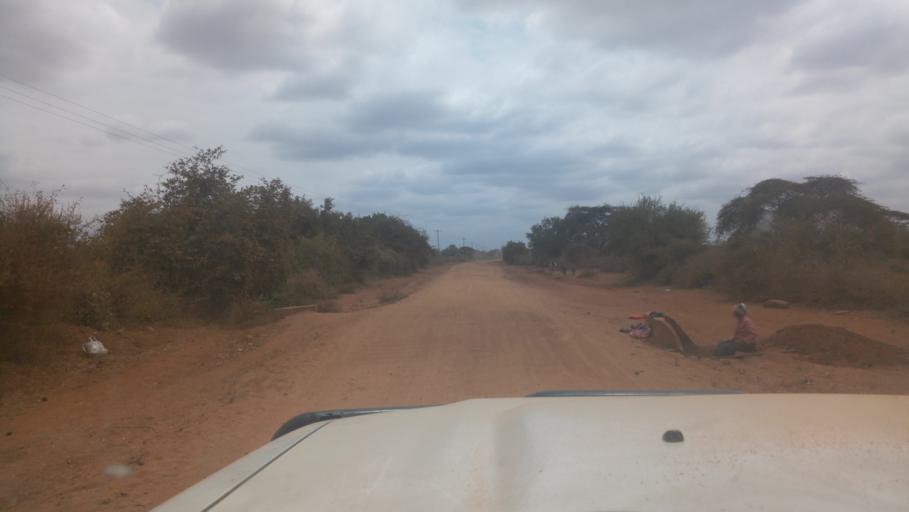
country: KE
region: Makueni
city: Wote
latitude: -1.8613
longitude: 37.9520
